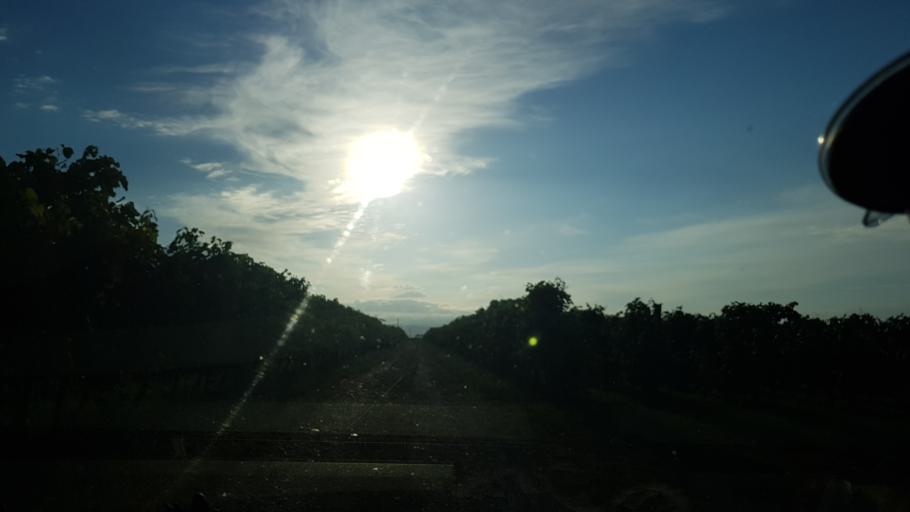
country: IT
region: Friuli Venezia Giulia
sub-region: Provincia di Udine
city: Chiopris
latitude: 45.9360
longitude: 13.3767
